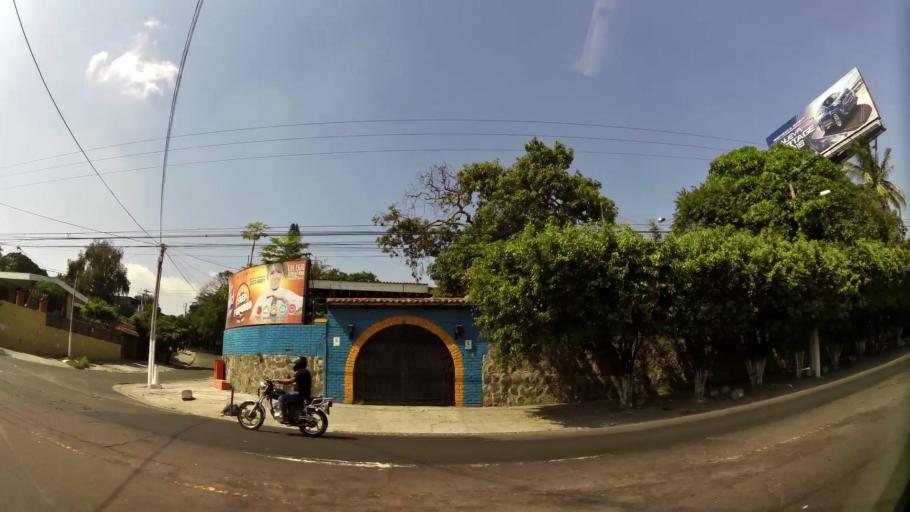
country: SV
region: San Salvador
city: San Salvador
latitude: 13.6914
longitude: -89.2223
